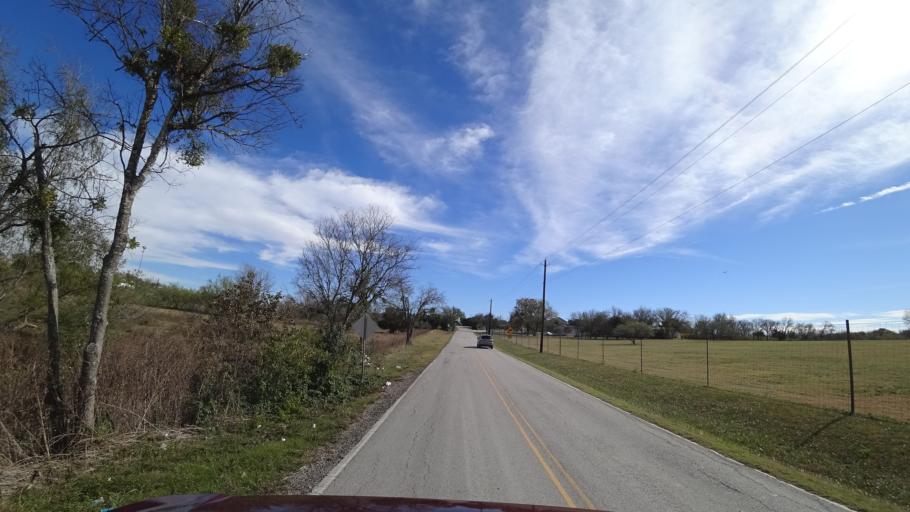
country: US
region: Texas
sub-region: Travis County
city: Onion Creek
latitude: 30.1167
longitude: -97.7491
